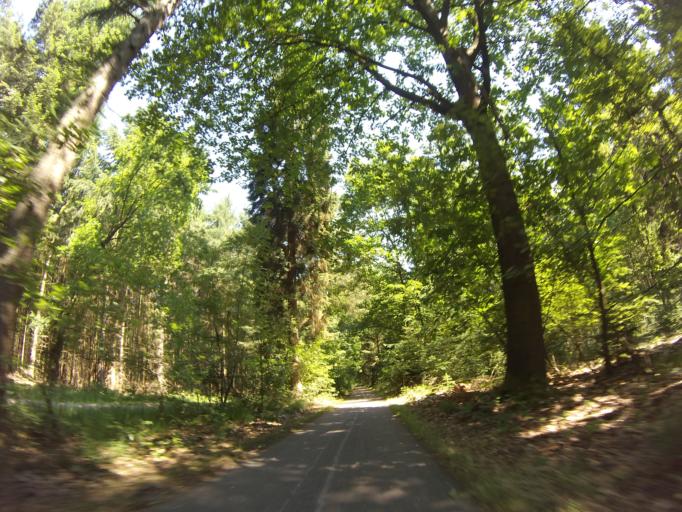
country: NL
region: Drenthe
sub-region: Gemeente Coevorden
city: Sleen
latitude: 52.8325
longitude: 6.7371
